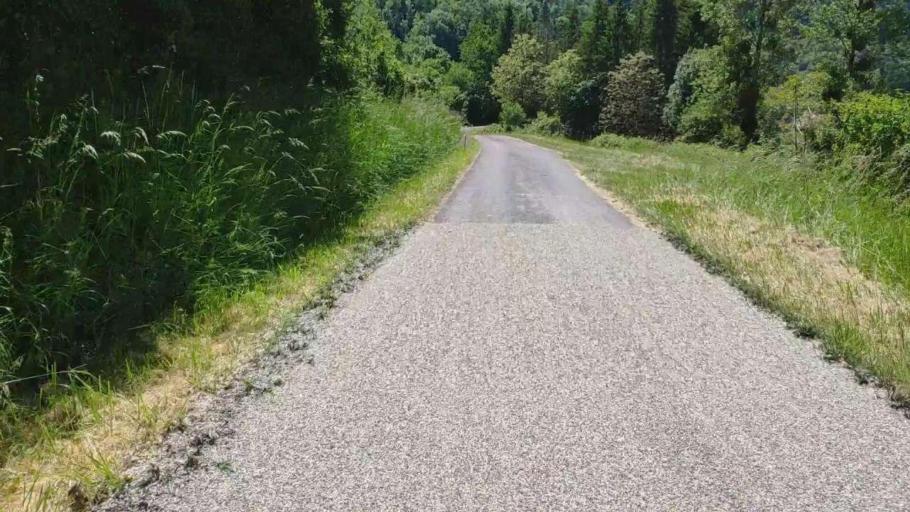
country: FR
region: Franche-Comte
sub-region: Departement du Jura
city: Poligny
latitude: 46.7517
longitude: 5.6741
